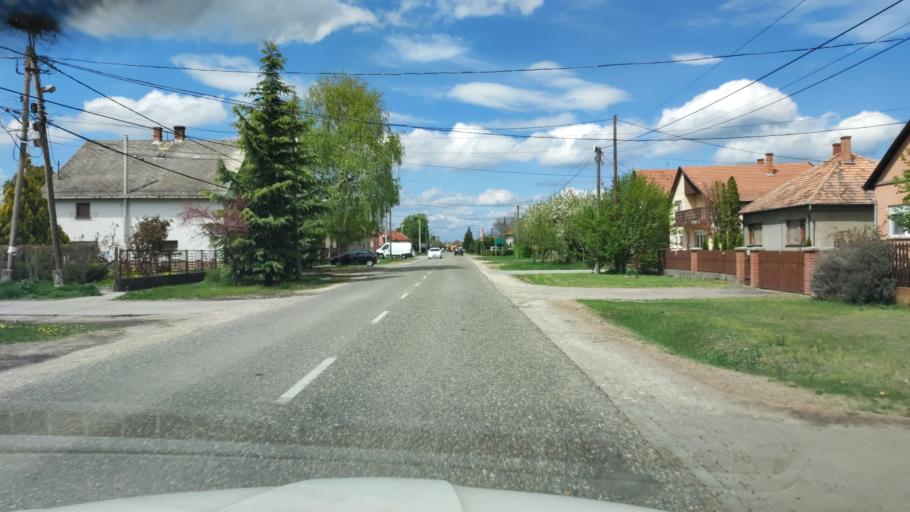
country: HU
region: Pest
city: Tortel
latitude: 47.1211
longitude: 19.9411
